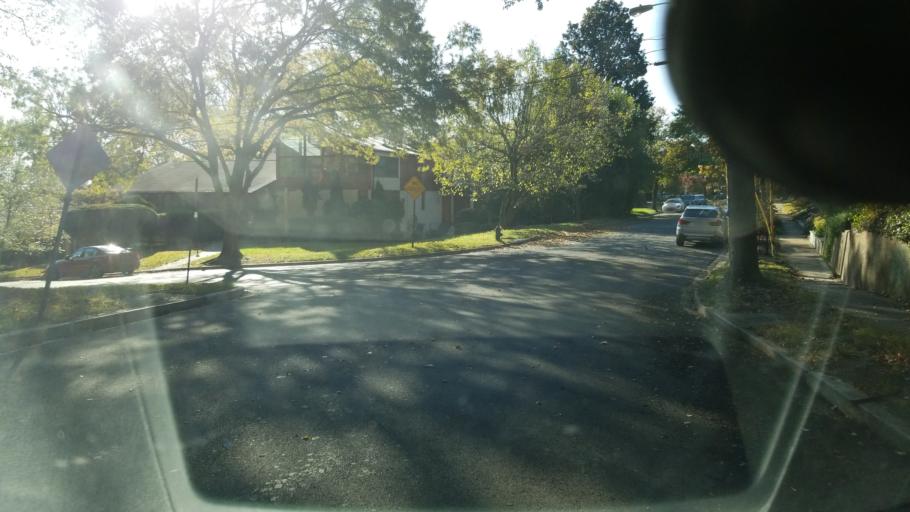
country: US
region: Maryland
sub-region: Montgomery County
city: Chevy Chase
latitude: 38.9548
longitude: -77.0611
